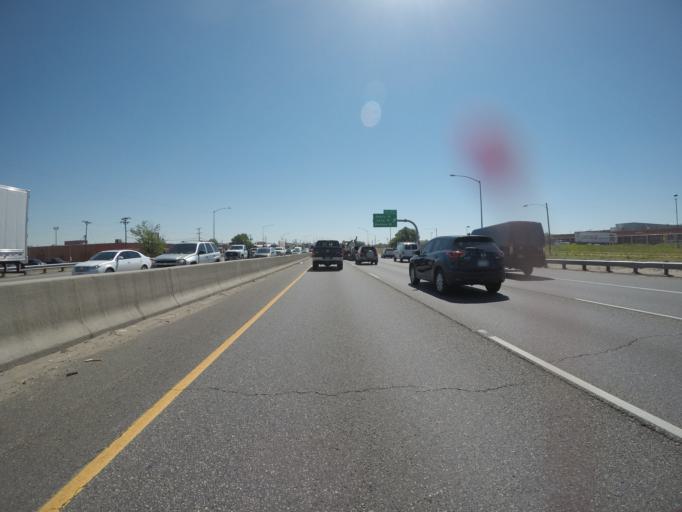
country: US
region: Colorado
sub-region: Adams County
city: Commerce City
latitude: 39.7800
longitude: -104.9380
